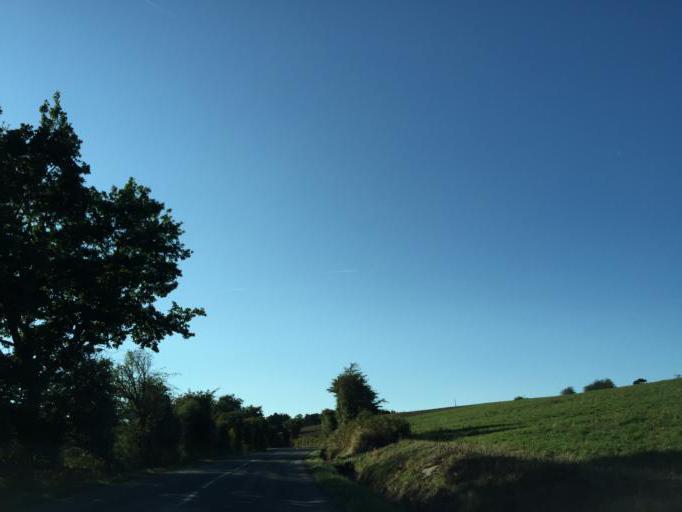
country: FR
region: Midi-Pyrenees
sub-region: Departement de l'Aveyron
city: Salles-Curan
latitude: 44.1298
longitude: 2.8894
